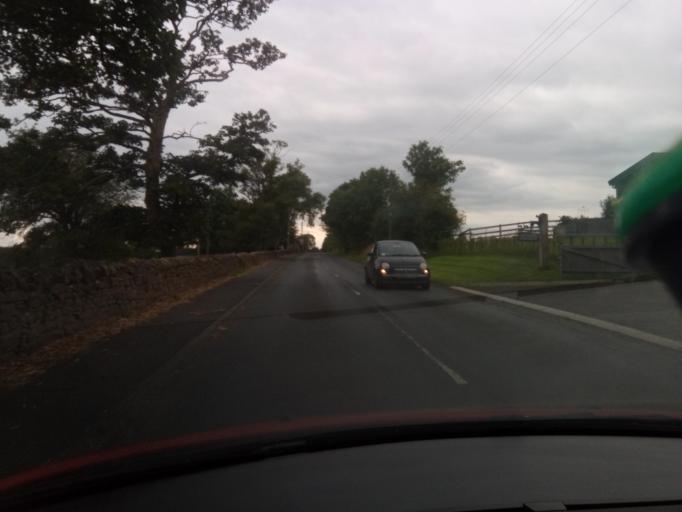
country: GB
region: England
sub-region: Northumberland
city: Warden
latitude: 54.9702
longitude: -2.1438
